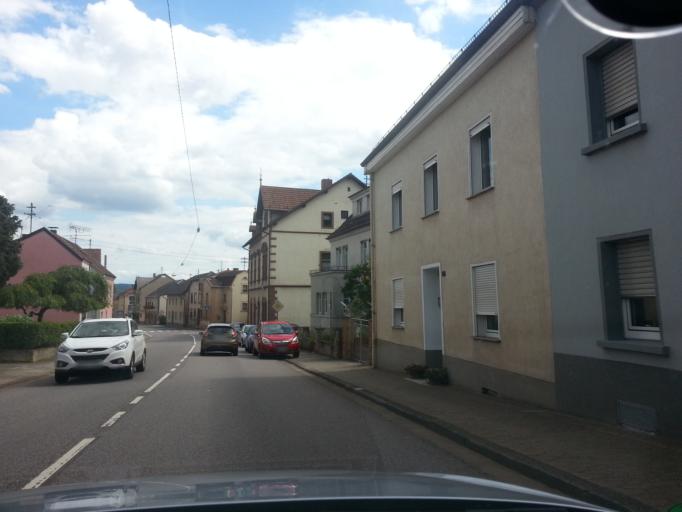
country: DE
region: Saarland
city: Mettlach
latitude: 49.4783
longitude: 6.6016
